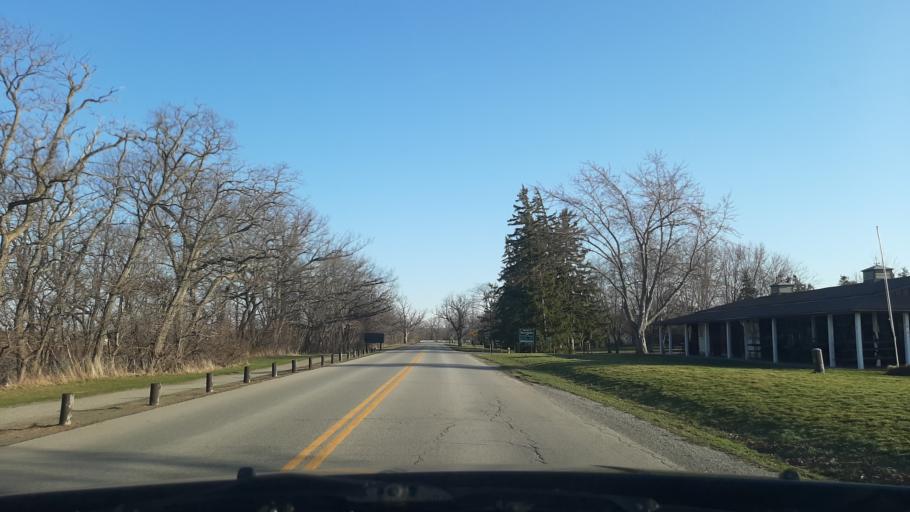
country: US
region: New York
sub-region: Niagara County
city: Youngstown
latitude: 43.2266
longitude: -79.0586
